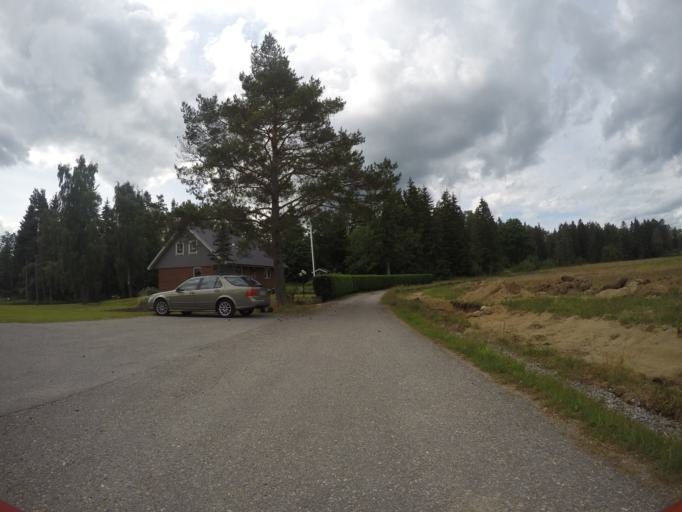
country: SE
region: Vaestra Goetaland
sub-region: Trollhattan
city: Trollhattan
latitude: 58.2257
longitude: 12.3107
